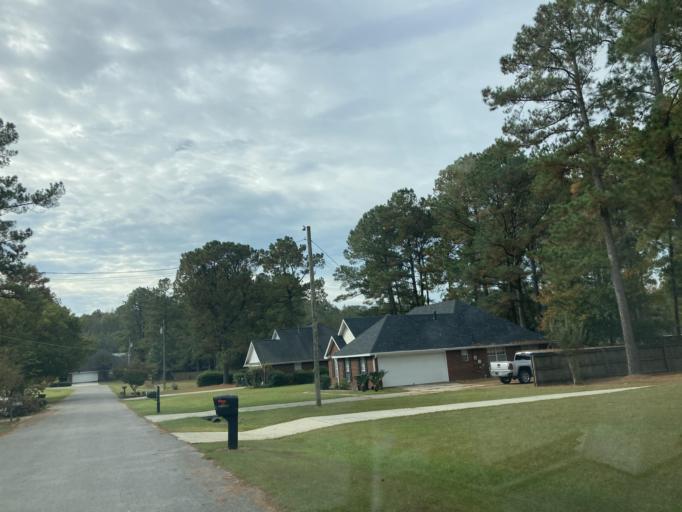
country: US
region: Mississippi
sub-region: Lamar County
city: West Hattiesburg
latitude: 31.2837
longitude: -89.3637
